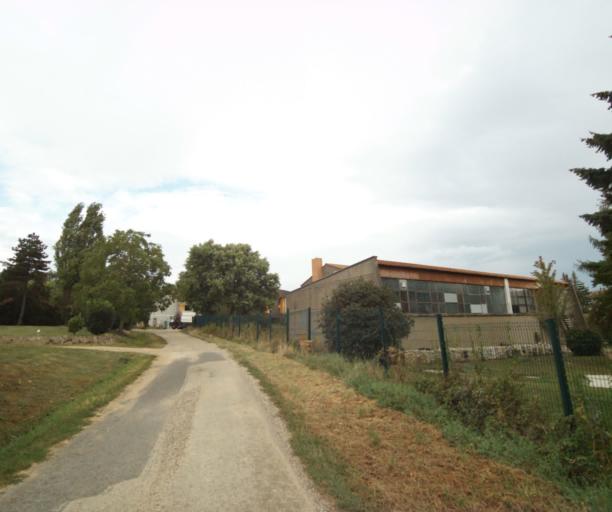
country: FR
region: Bourgogne
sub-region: Departement de Saone-et-Loire
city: Tournus
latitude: 46.5659
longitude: 4.8919
